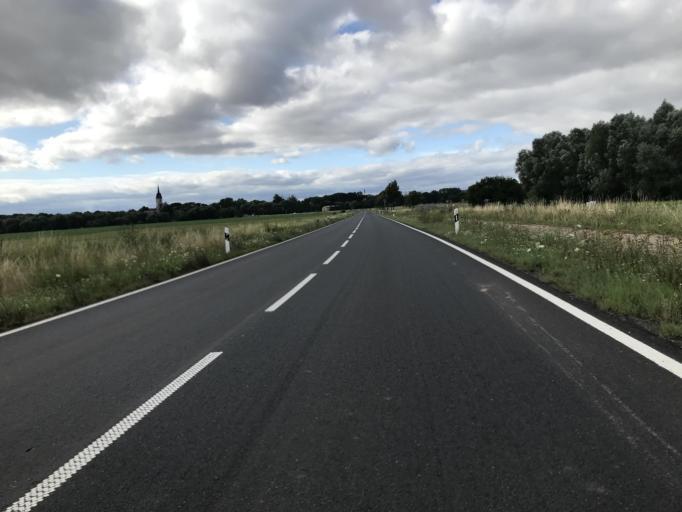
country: DE
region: Saxony-Anhalt
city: Ditfurt
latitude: 51.8223
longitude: 11.2123
